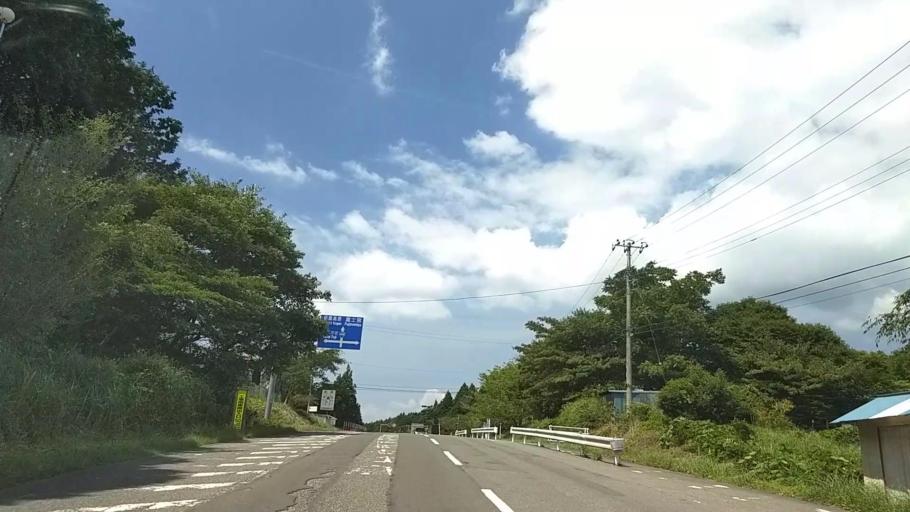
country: JP
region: Shizuoka
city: Fuji
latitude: 35.2479
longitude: 138.7105
